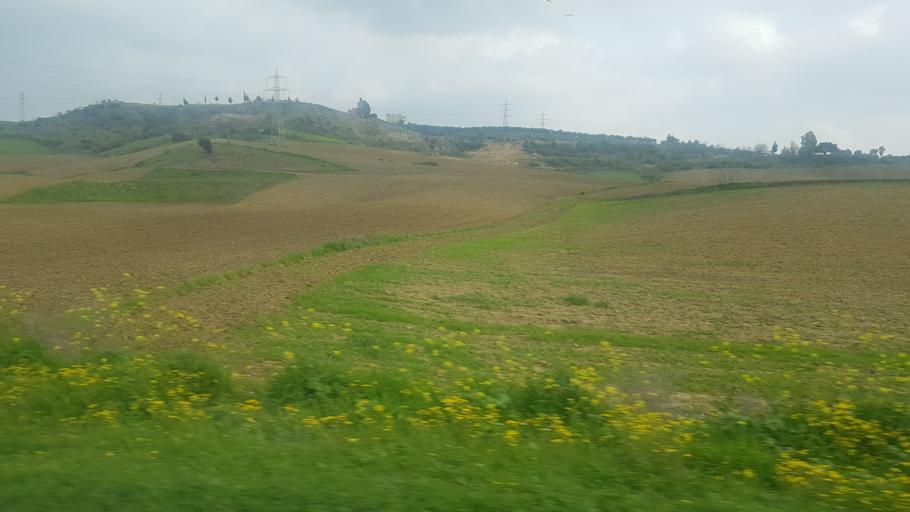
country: TR
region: Mersin
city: Yenice
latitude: 37.0599
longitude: 35.1691
